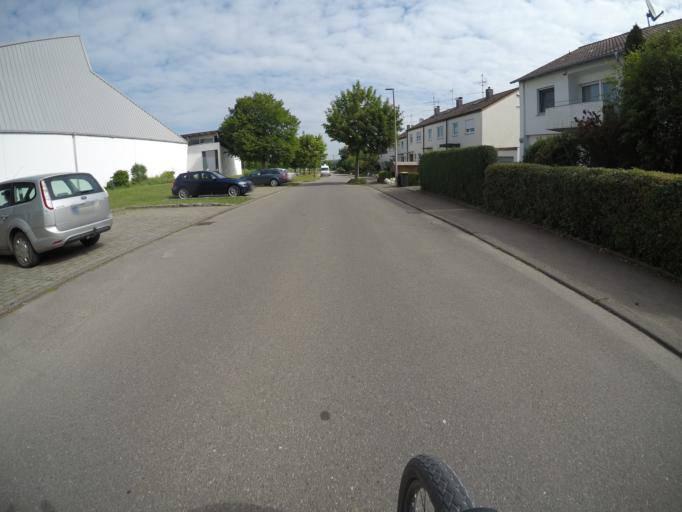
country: DE
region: Baden-Wuerttemberg
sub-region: Regierungsbezirk Stuttgart
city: Unterensingen
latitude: 48.6611
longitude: 9.3543
